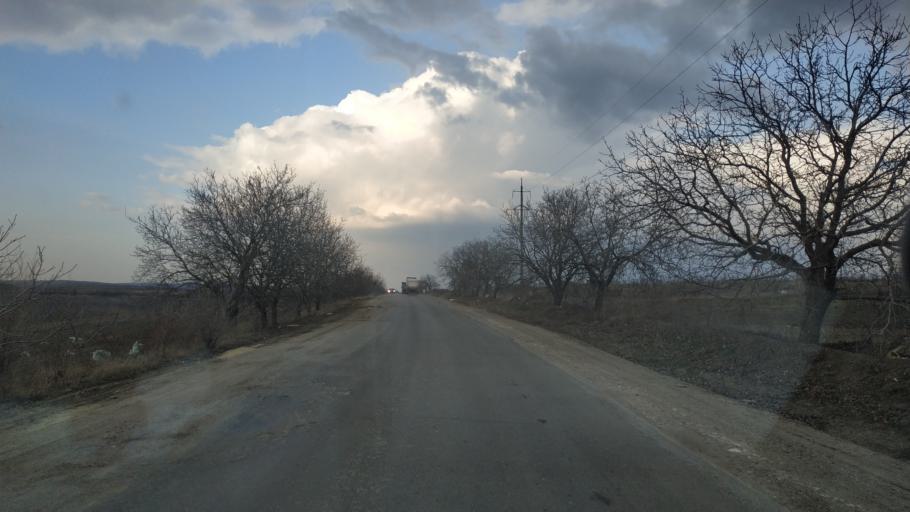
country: MD
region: Anenii Noi
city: Anenii Noi
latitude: 46.9624
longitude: 29.2846
